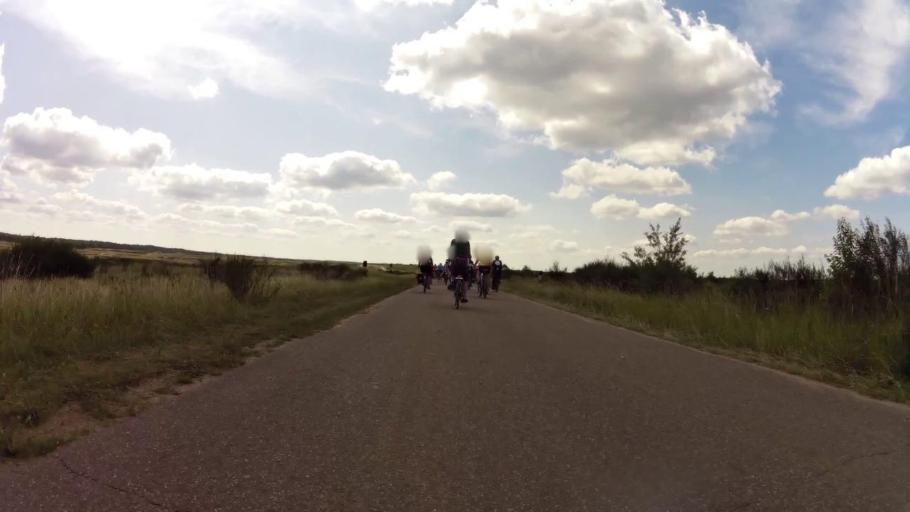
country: PL
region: West Pomeranian Voivodeship
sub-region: Powiat drawski
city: Drawsko Pomorskie
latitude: 53.4305
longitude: 15.7611
